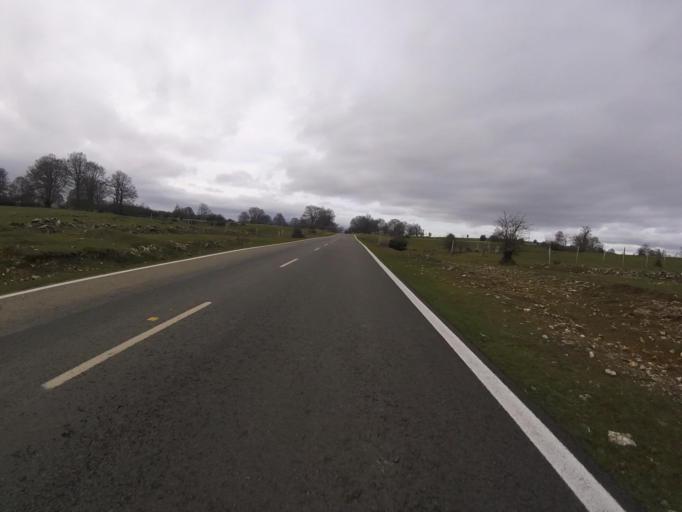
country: ES
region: Navarre
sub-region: Provincia de Navarra
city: Eulate
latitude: 42.7994
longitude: -2.1445
